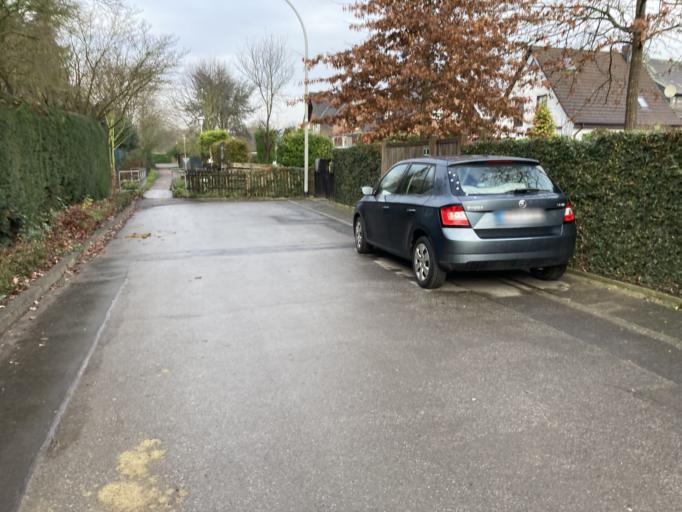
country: DE
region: North Rhine-Westphalia
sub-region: Regierungsbezirk Dusseldorf
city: Neubrueck
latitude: 51.1208
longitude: 6.6228
